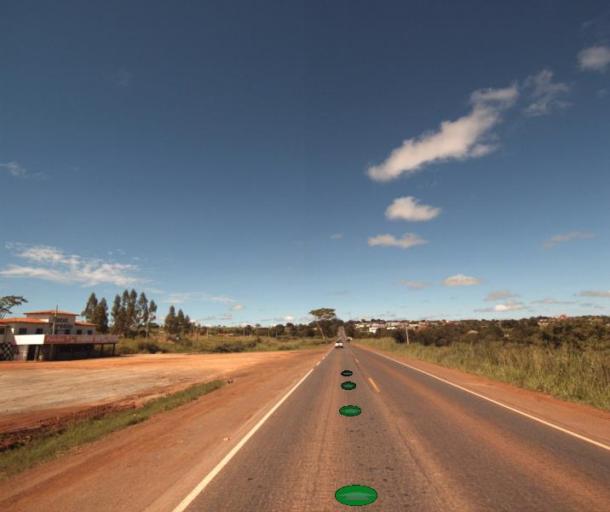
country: BR
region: Goias
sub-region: Rialma
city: Rialma
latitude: -15.3036
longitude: -49.5707
